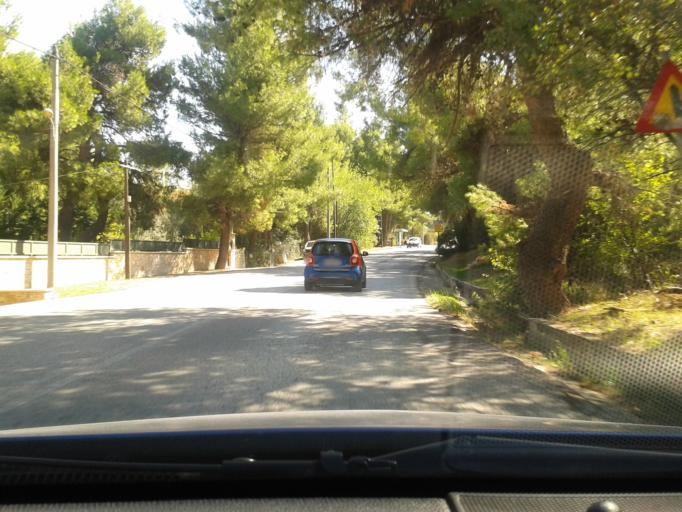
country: GR
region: Attica
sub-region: Nomarchia Anatolikis Attikis
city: Dionysos
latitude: 38.0994
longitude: 23.8873
